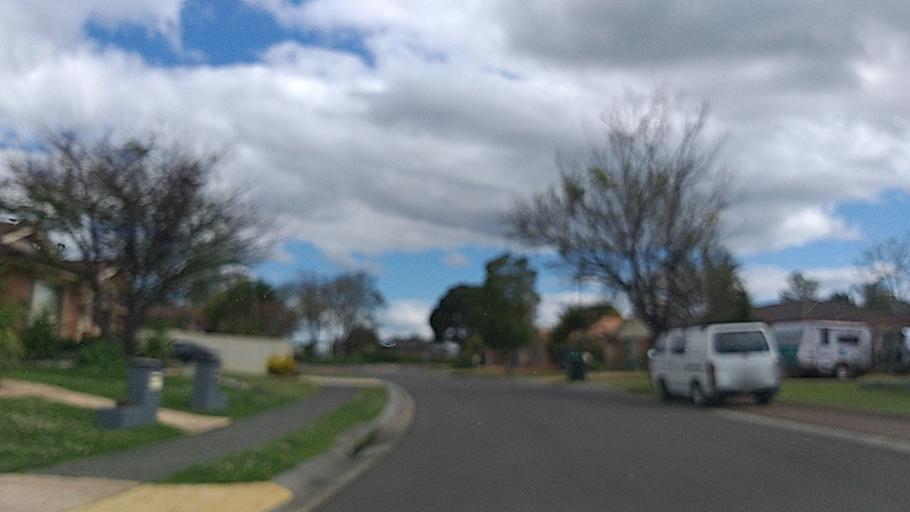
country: AU
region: New South Wales
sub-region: Wollongong
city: Dapto
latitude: -34.4865
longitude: 150.7745
